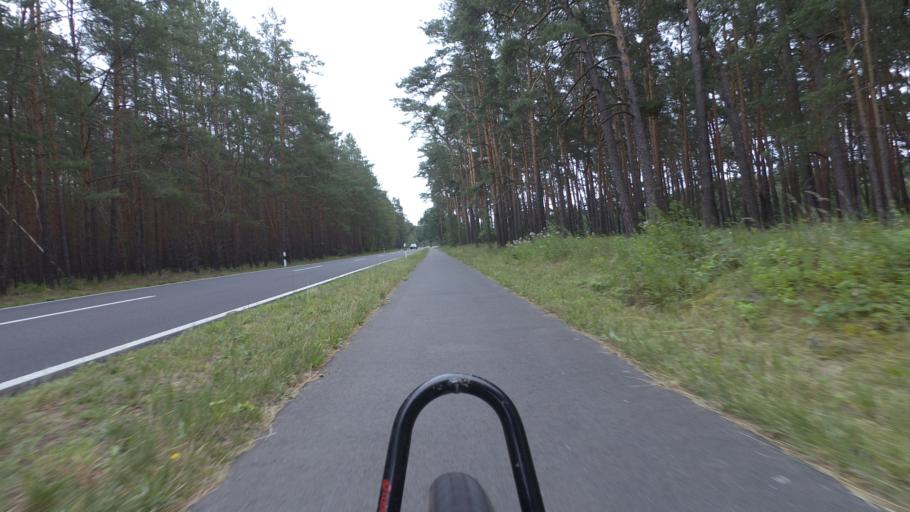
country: DE
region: Brandenburg
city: Sperenberg
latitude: 52.0859
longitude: 13.2925
